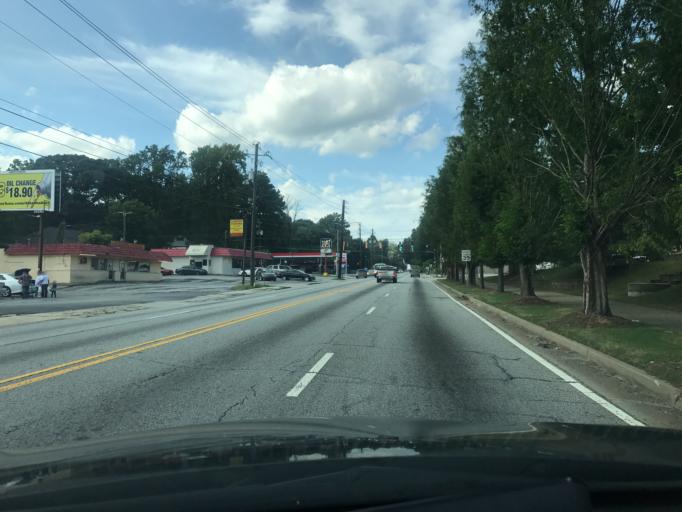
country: US
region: Georgia
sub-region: DeKalb County
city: Gresham Park
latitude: 33.7230
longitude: -84.3494
